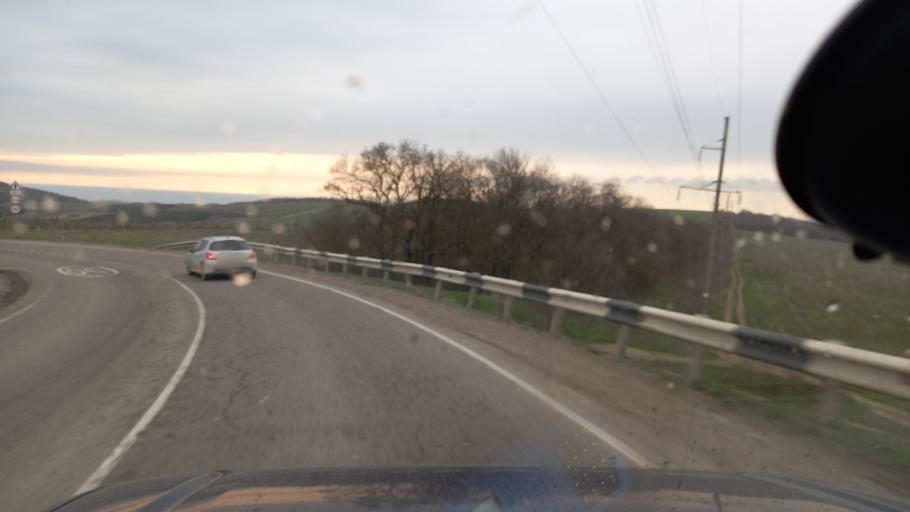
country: RU
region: Krasnodarskiy
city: Sukko
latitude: 44.8413
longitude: 37.4009
